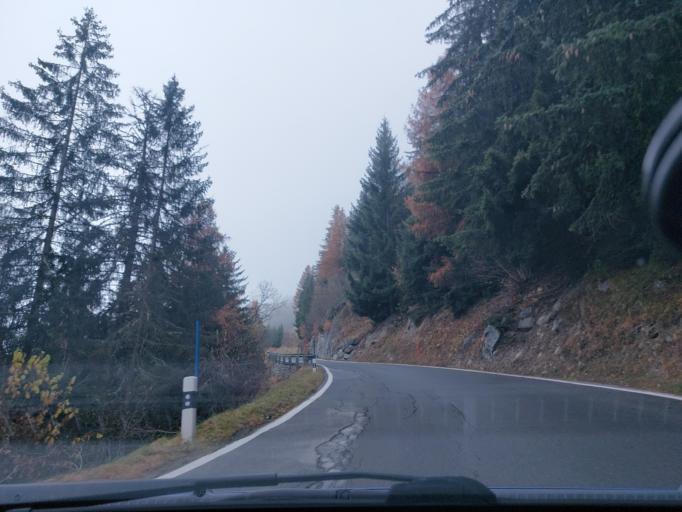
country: CH
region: Valais
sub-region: Conthey District
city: Basse-Nendaz
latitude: 46.1653
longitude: 7.3125
